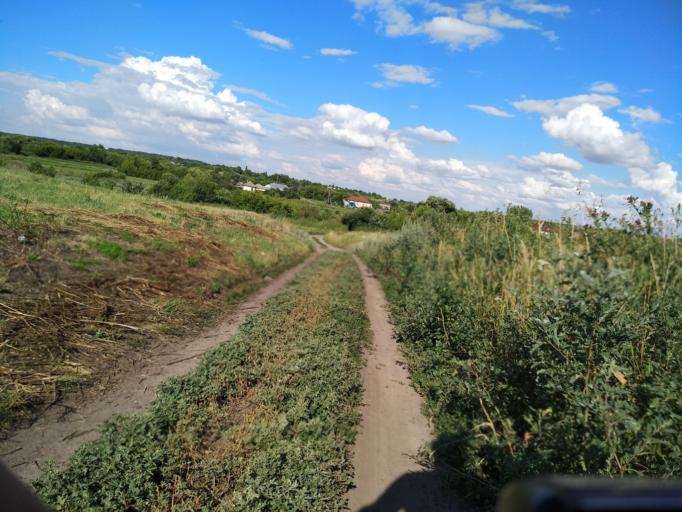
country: RU
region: Lipetsk
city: Dobrinka
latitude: 52.0348
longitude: 40.5603
